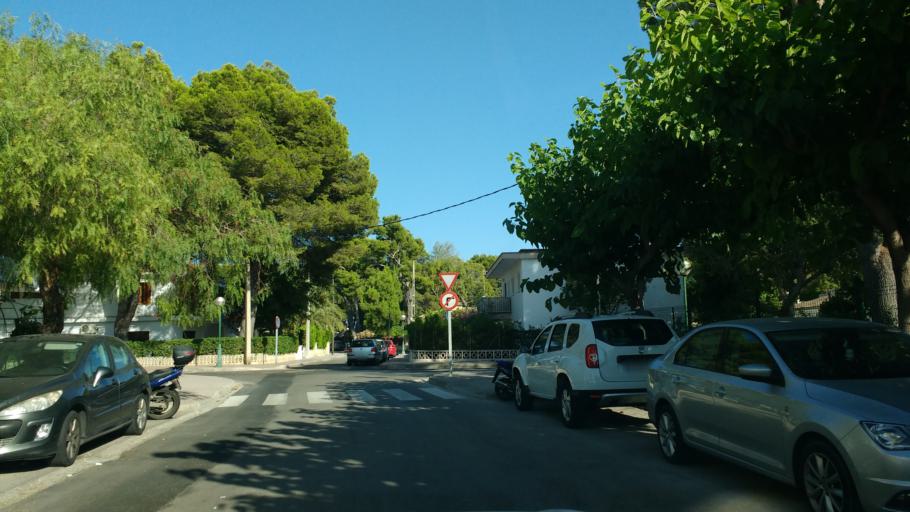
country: ES
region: Balearic Islands
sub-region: Illes Balears
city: Port d'Alcudia
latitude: 39.8371
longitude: 3.1202
